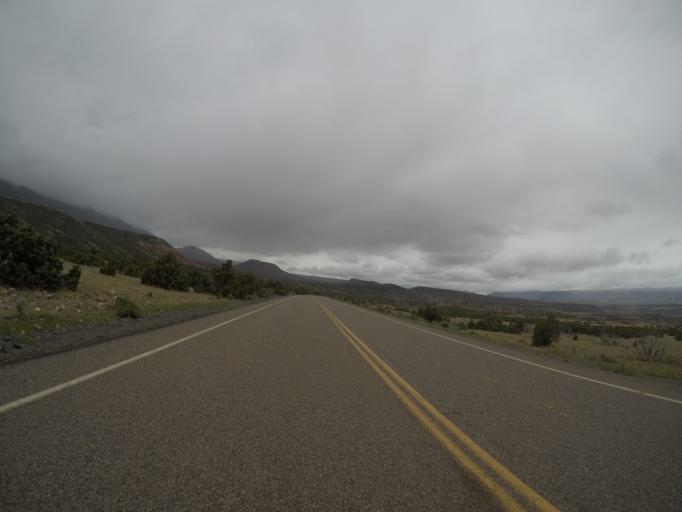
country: US
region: Wyoming
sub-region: Big Horn County
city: Lovell
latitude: 45.0944
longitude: -108.2500
